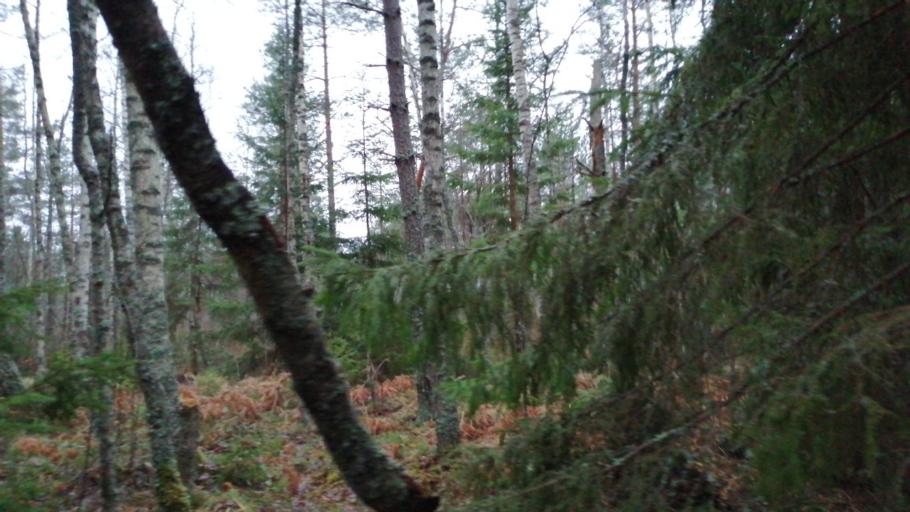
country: EE
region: Polvamaa
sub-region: Polva linn
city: Polva
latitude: 58.1532
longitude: 27.0687
